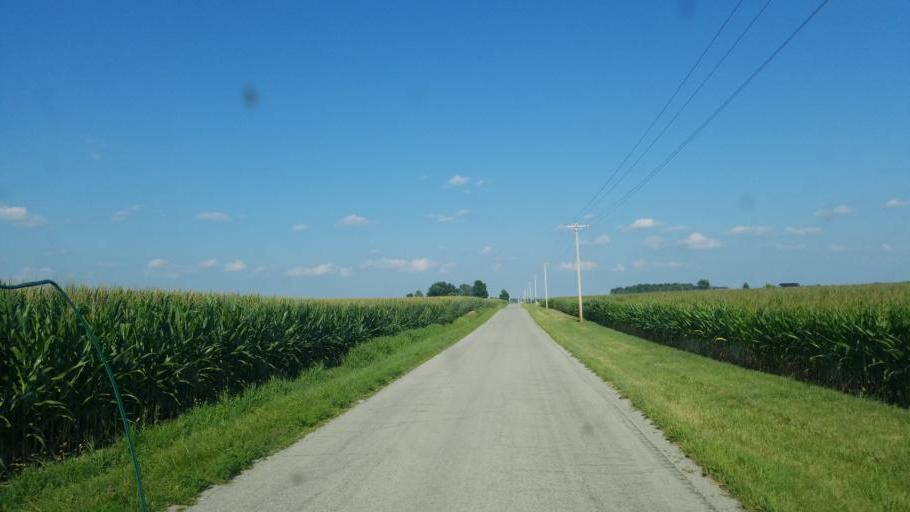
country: US
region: Ohio
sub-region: Wyandot County
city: Upper Sandusky
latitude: 40.7893
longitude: -83.1573
